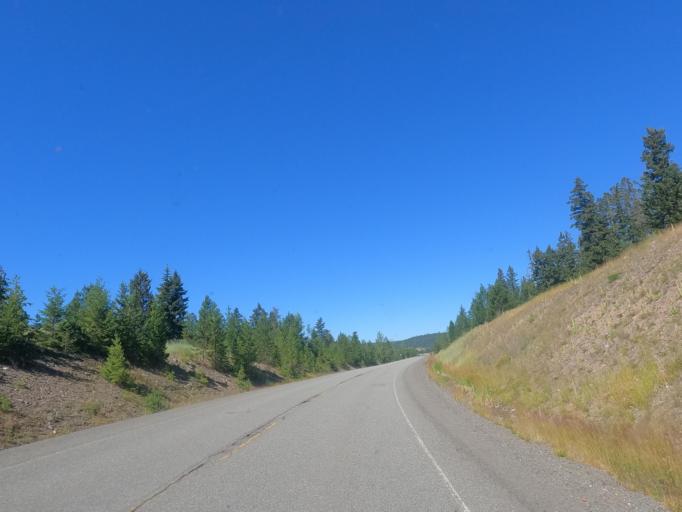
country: CA
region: British Columbia
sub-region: Thompson-Nicola Regional District
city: Ashcroft
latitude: 50.5709
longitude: -121.1428
